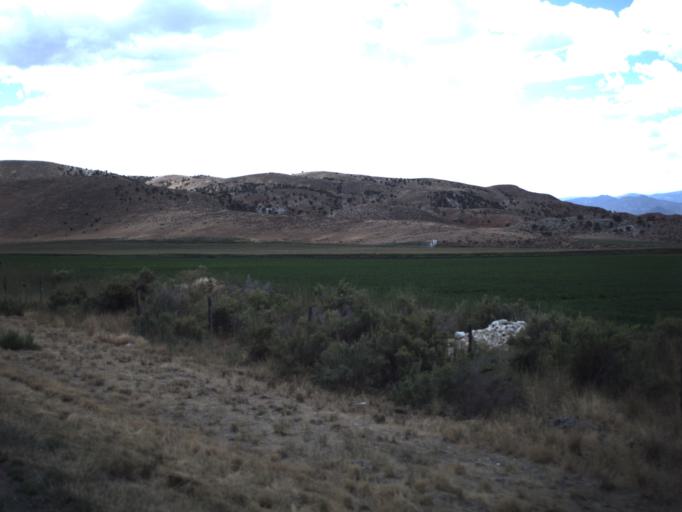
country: US
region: Utah
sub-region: Sanpete County
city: Gunnison
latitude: 39.1690
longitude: -111.7051
